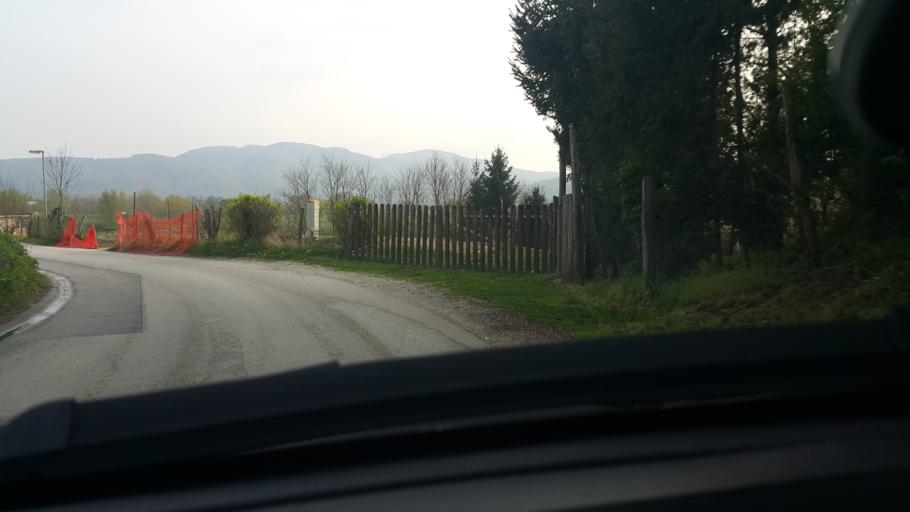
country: SI
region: Brezice
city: Brezice
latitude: 45.9103
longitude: 15.6271
